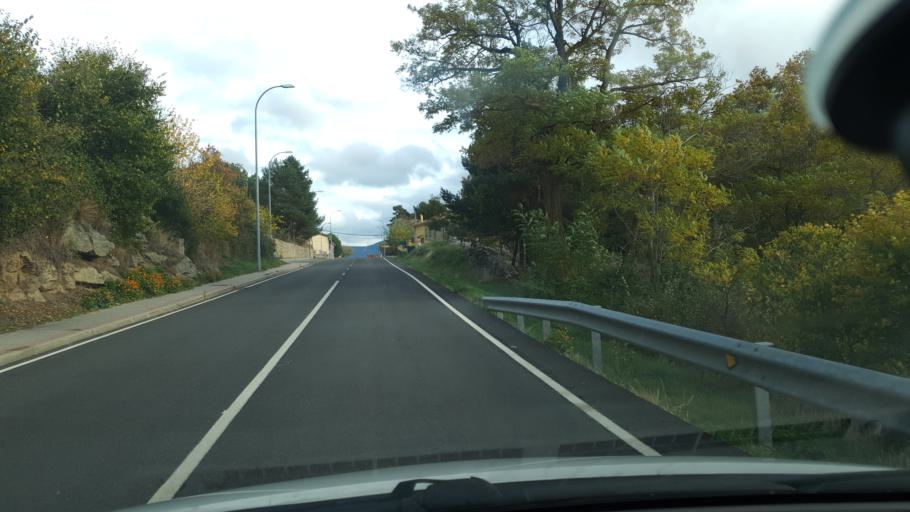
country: ES
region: Castille and Leon
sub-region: Provincia de Avila
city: Hoyocasero
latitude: 40.3986
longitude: -4.9775
